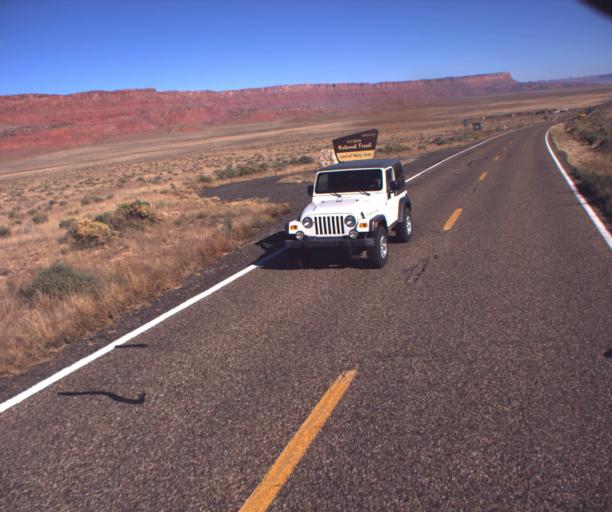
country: US
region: Arizona
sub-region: Coconino County
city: Fredonia
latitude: 36.7335
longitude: -112.0569
